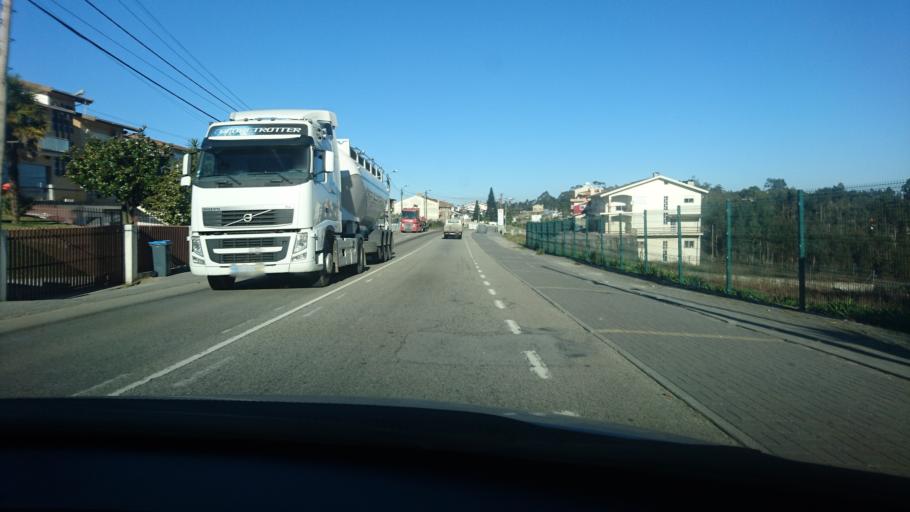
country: PT
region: Aveiro
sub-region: Santa Maria da Feira
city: Arrifana
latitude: 40.9370
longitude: -8.5070
